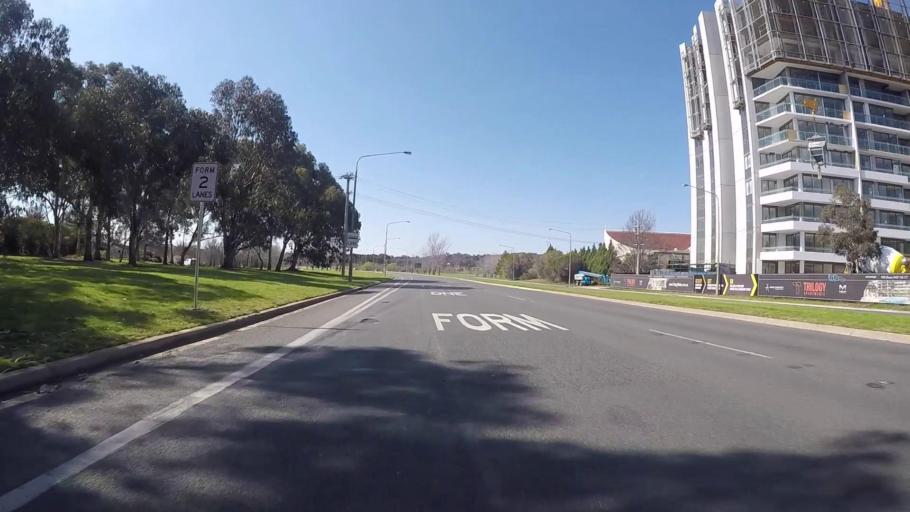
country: AU
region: Australian Capital Territory
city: Forrest
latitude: -35.3382
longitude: 149.0837
